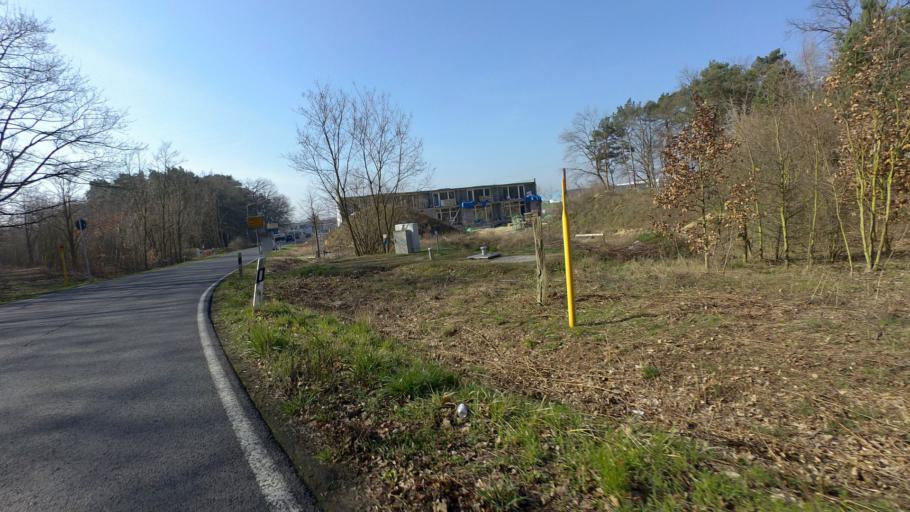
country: DE
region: Berlin
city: Lichtenrade
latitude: 52.3619
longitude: 13.4417
